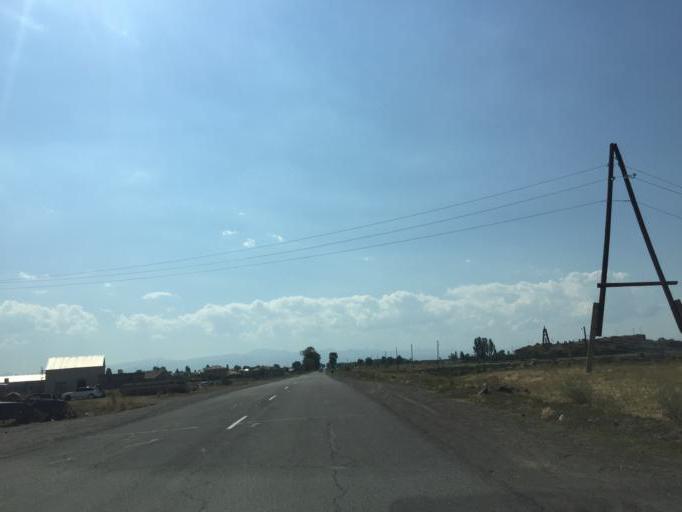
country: AM
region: Geghark'unik'i Marz
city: Tsovinar
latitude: 40.1624
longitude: 45.4773
